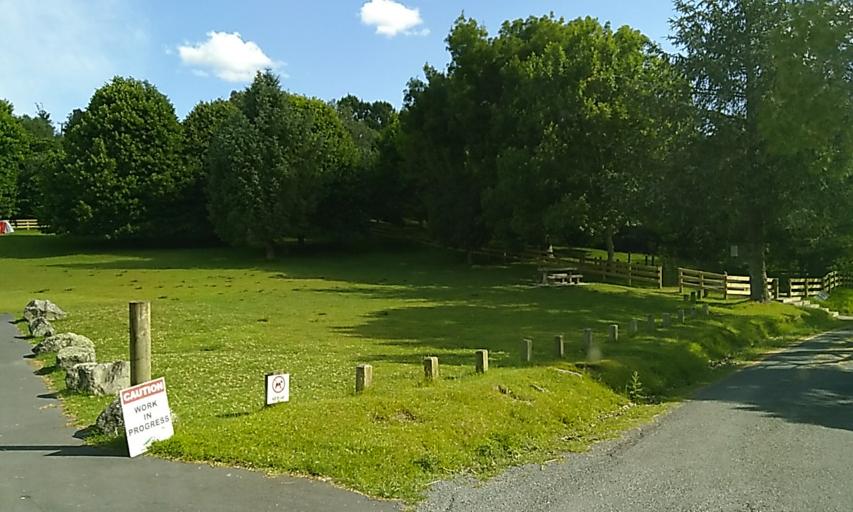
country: NZ
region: Bay of Plenty
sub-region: Tauranga City
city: Tauranga
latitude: -37.8146
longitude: 176.0446
